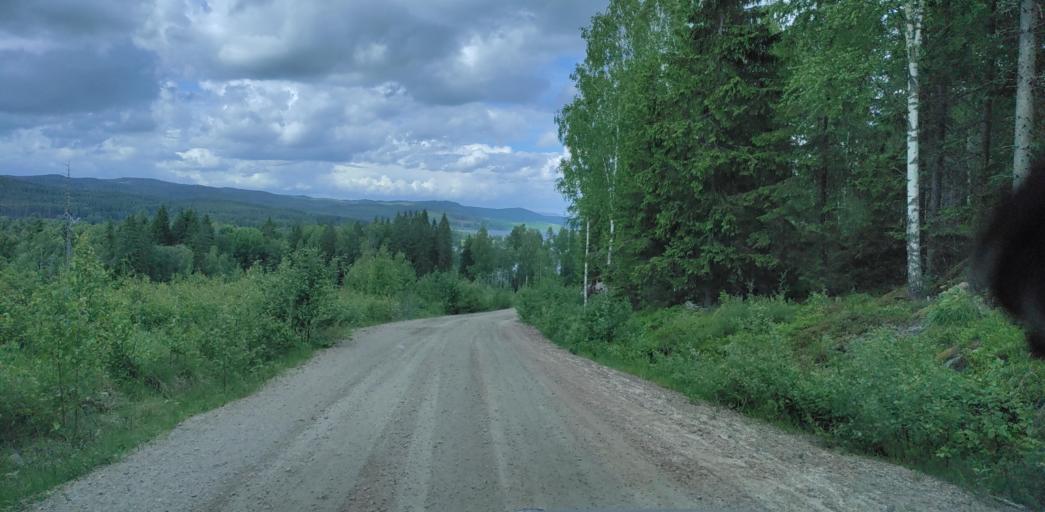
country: SE
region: Vaermland
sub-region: Munkfors Kommun
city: Munkfors
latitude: 59.9659
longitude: 13.4233
